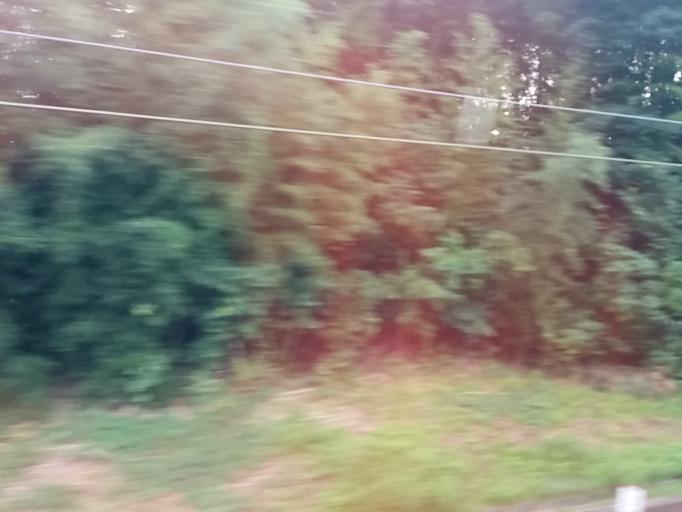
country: JP
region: Kyoto
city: Tanabe
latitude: 34.8178
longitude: 135.7726
